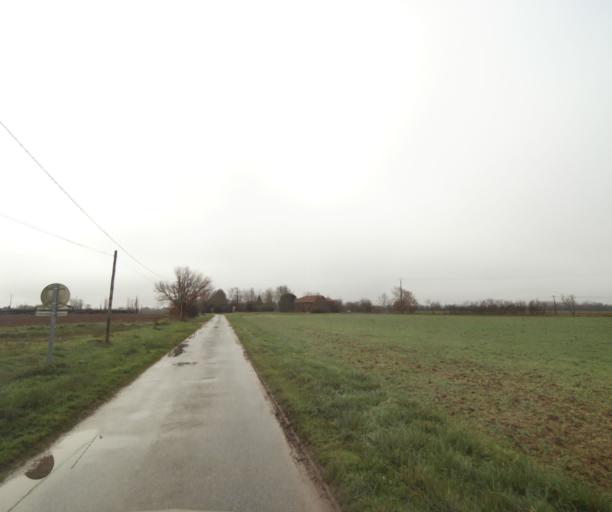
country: FR
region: Midi-Pyrenees
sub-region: Departement de la Haute-Garonne
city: Villemur-sur-Tarn
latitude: 43.8891
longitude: 1.4767
